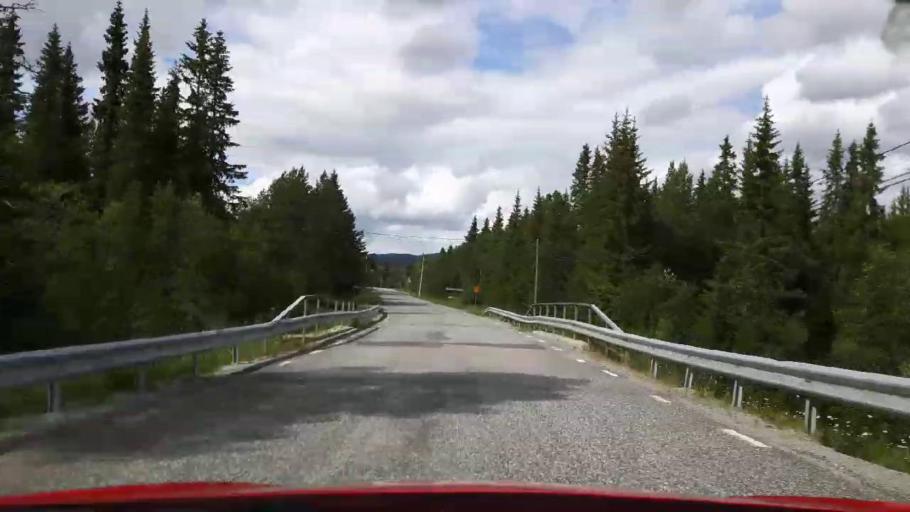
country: NO
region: Hedmark
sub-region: Engerdal
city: Engerdal
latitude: 62.4260
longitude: 12.6861
